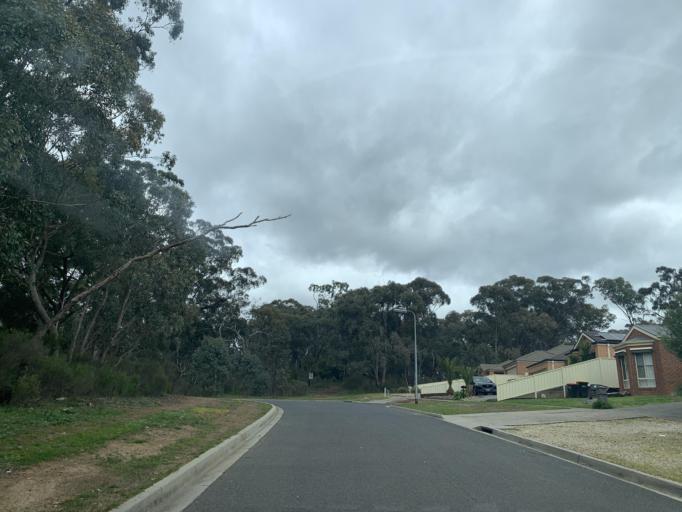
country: AU
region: Victoria
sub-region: Whittlesea
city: Whittlesea
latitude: -37.2124
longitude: 145.0432
